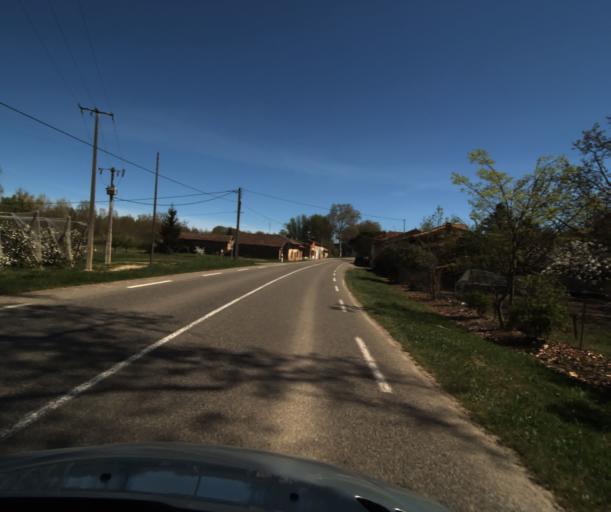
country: FR
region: Midi-Pyrenees
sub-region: Departement du Tarn-et-Garonne
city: Lafrancaise
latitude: 44.1346
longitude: 1.1946
